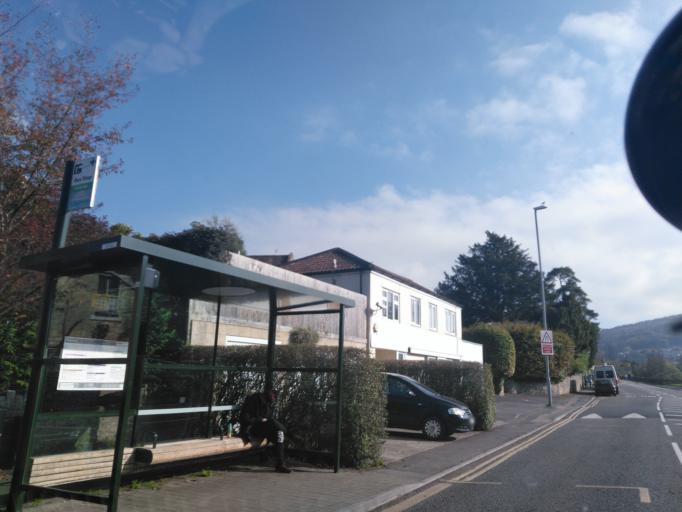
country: GB
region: England
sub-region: Bath and North East Somerset
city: Bath
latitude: 51.4050
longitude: -2.3164
